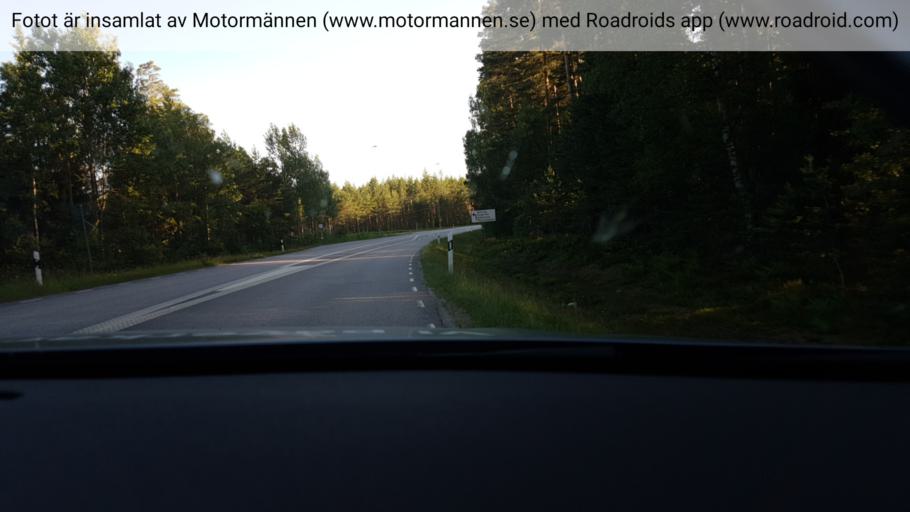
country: SE
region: Vaestra Goetaland
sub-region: Skovde Kommun
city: Stopen
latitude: 58.4541
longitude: 13.9542
